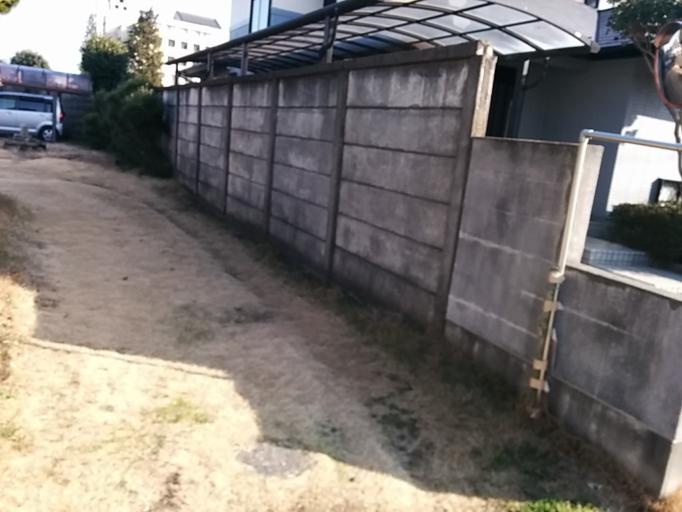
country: JP
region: Saitama
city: Kawagoe
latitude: 35.9218
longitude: 139.4774
